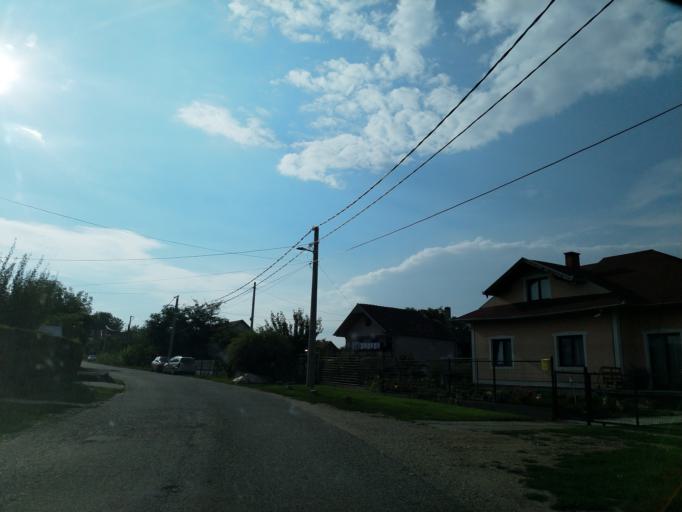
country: RS
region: Central Serbia
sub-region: Pomoravski Okrug
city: Jagodina
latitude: 43.9764
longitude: 21.2429
